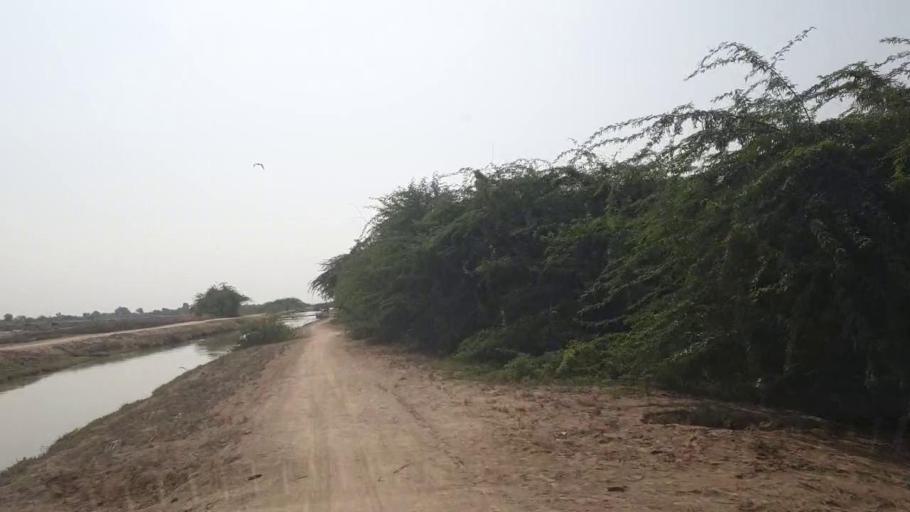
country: PK
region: Sindh
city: Kadhan
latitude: 24.5071
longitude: 68.8502
